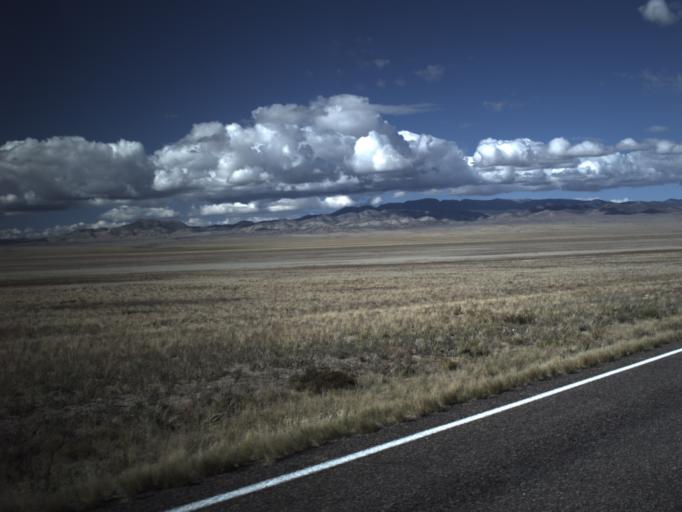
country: US
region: Utah
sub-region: Beaver County
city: Milford
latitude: 38.5174
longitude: -113.6415
